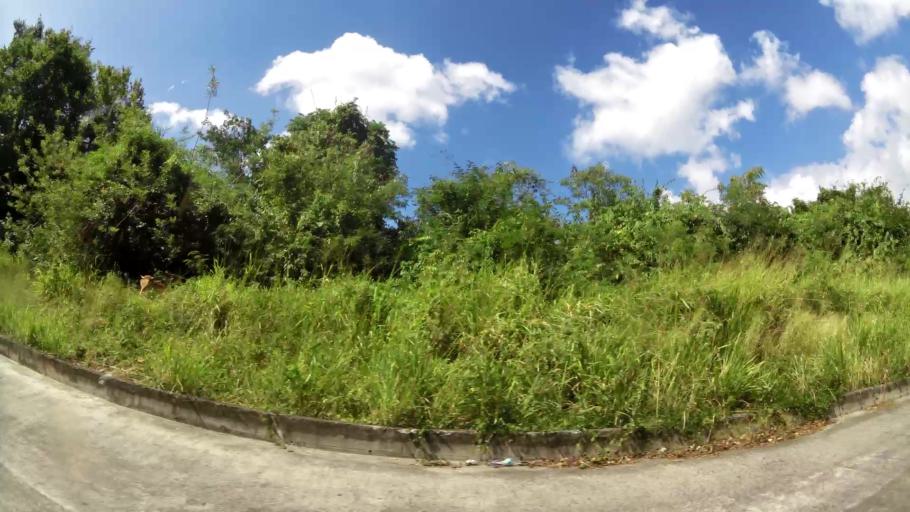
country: MQ
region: Martinique
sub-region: Martinique
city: Saint-Pierre
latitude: 14.6773
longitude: -61.1656
